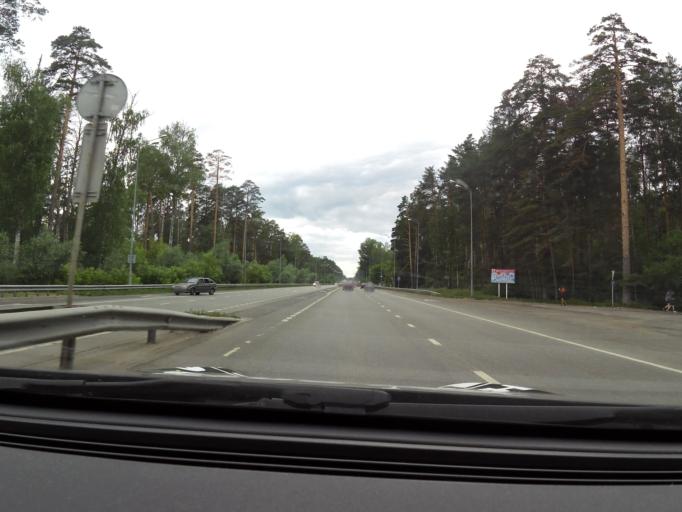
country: RU
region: Tatarstan
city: Staroye Arakchino
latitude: 55.8384
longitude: 48.9625
